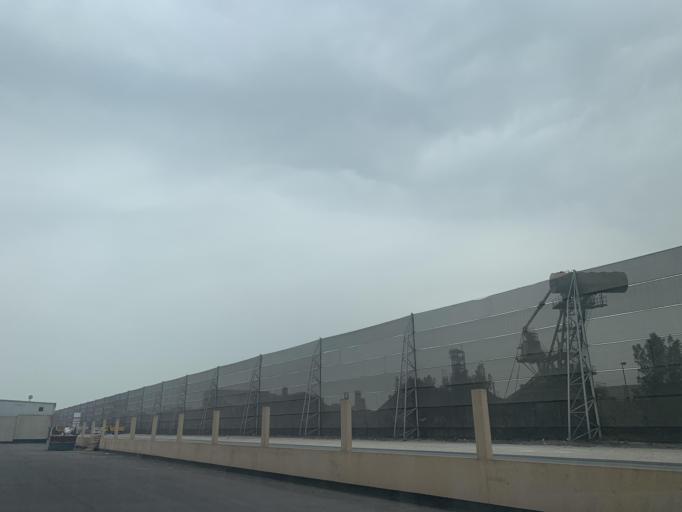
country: BH
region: Muharraq
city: Al Hadd
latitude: 26.2043
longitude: 50.6819
